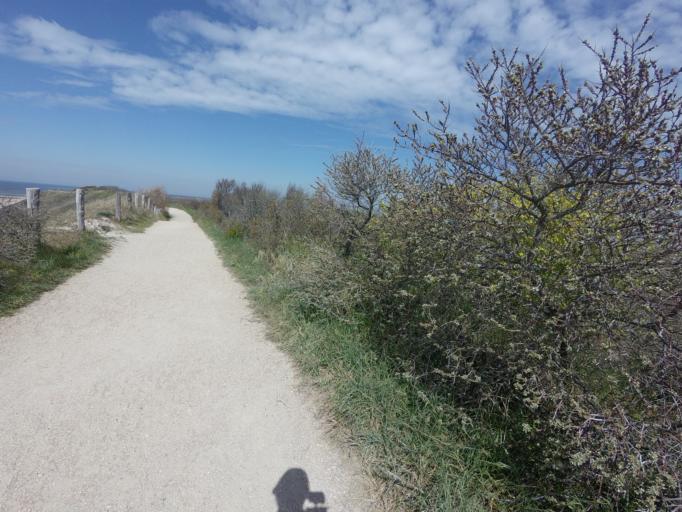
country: NL
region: Zeeland
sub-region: Gemeente Vlissingen
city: Vlissingen
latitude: 51.5096
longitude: 3.4620
